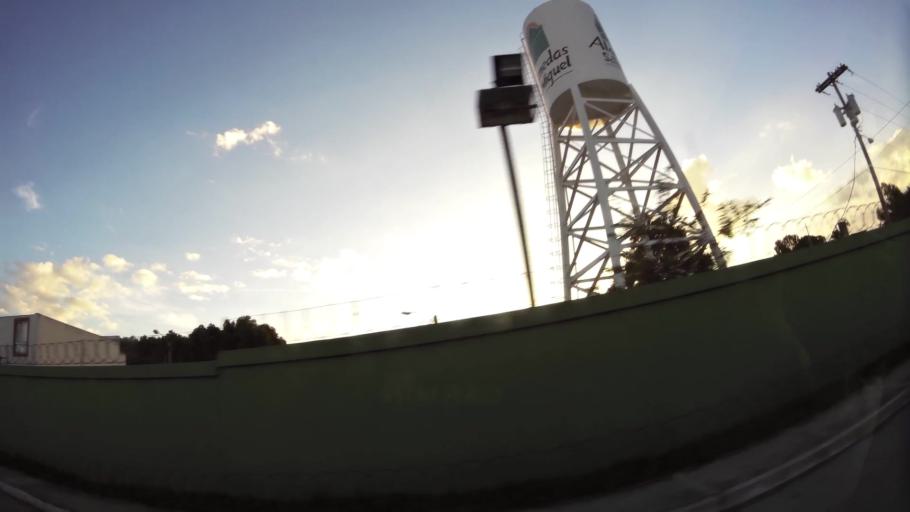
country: GT
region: Guatemala
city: Villa Nueva
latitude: 14.5061
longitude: -90.5773
